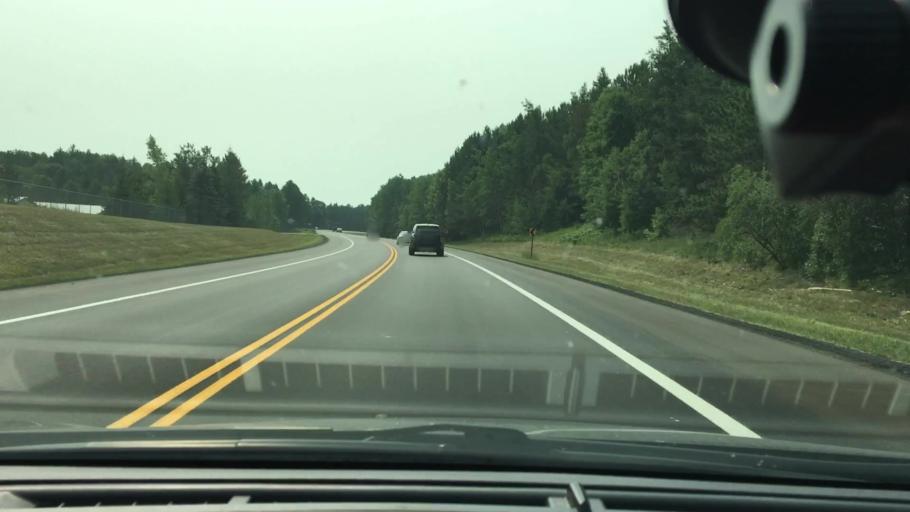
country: US
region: Minnesota
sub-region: Crow Wing County
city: Brainerd
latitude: 46.4167
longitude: -94.1785
